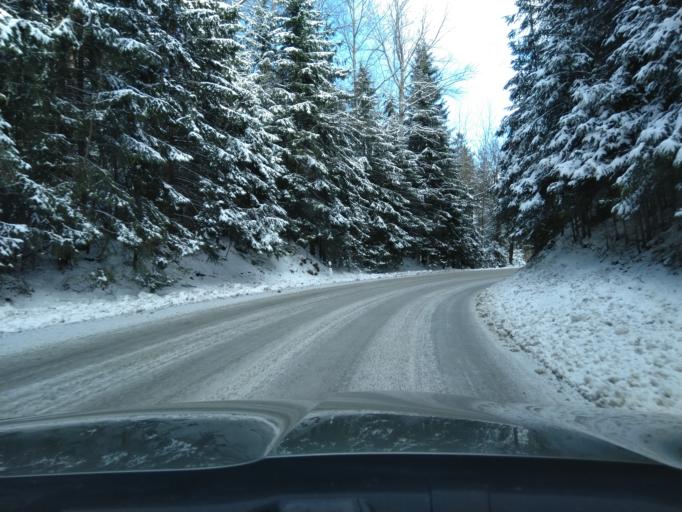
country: CZ
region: Jihocesky
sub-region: Okres Prachatice
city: Zdikov
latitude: 49.0568
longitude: 13.6953
